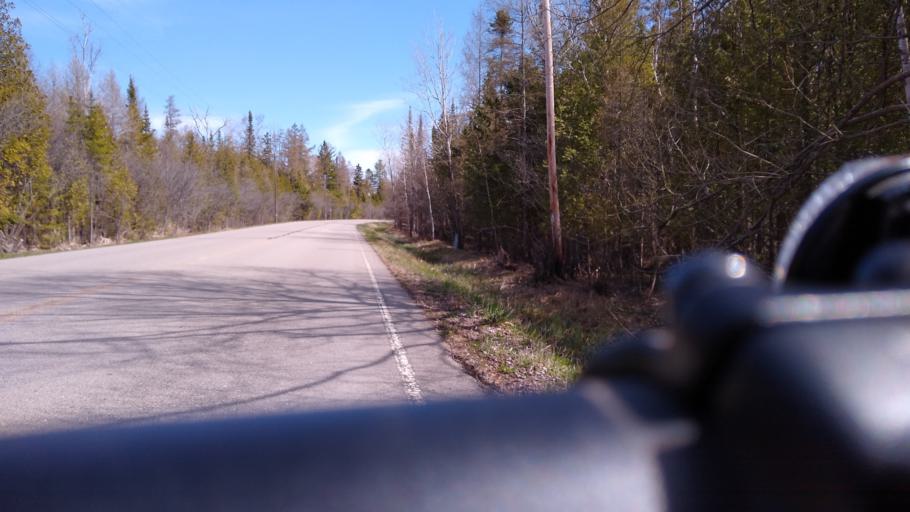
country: US
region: Michigan
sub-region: Delta County
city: Escanaba
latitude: 45.6843
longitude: -87.1481
